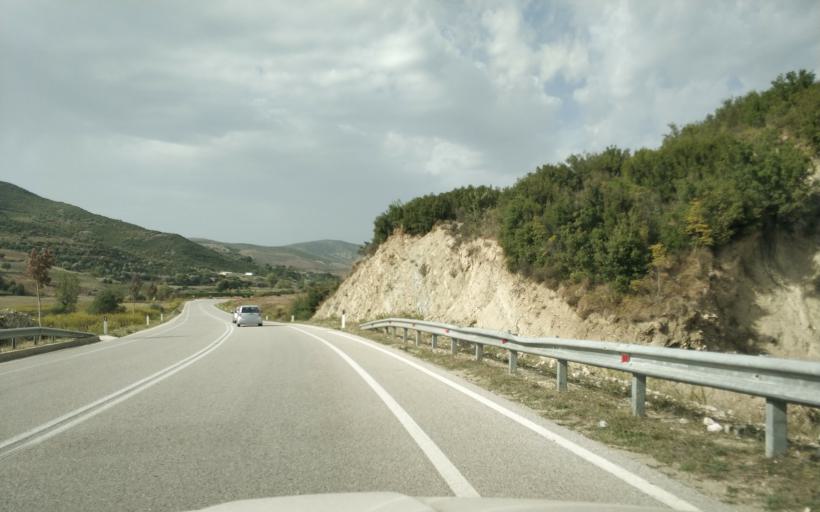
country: AL
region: Gjirokaster
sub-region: Rrethi i Tepelenes
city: Krahes
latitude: 40.4029
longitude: 19.8632
